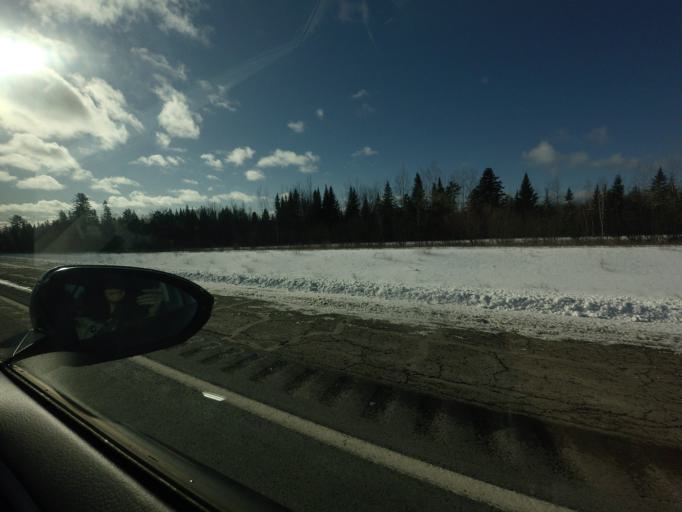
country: CA
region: New Brunswick
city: Fredericton
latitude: 45.8916
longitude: -66.6455
